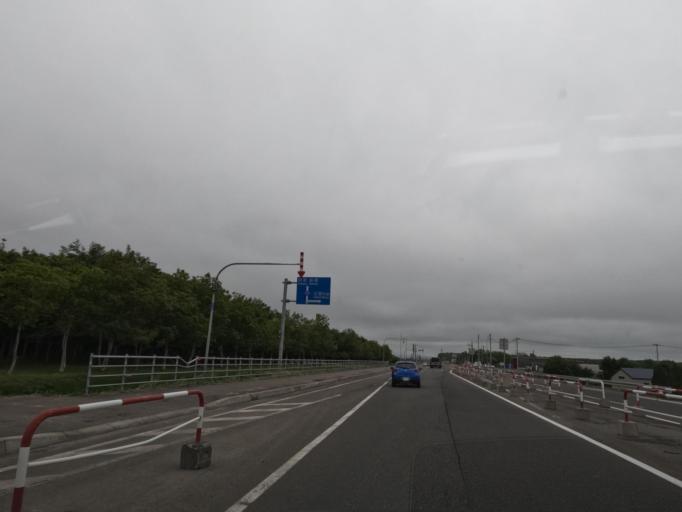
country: JP
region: Hokkaido
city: Ebetsu
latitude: 43.1438
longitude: 141.5167
